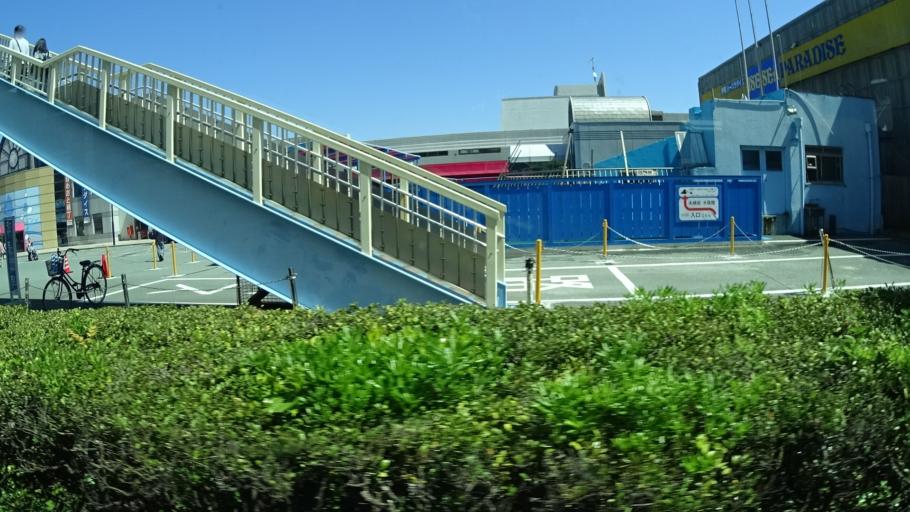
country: JP
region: Mie
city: Toba
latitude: 34.5073
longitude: 136.7911
